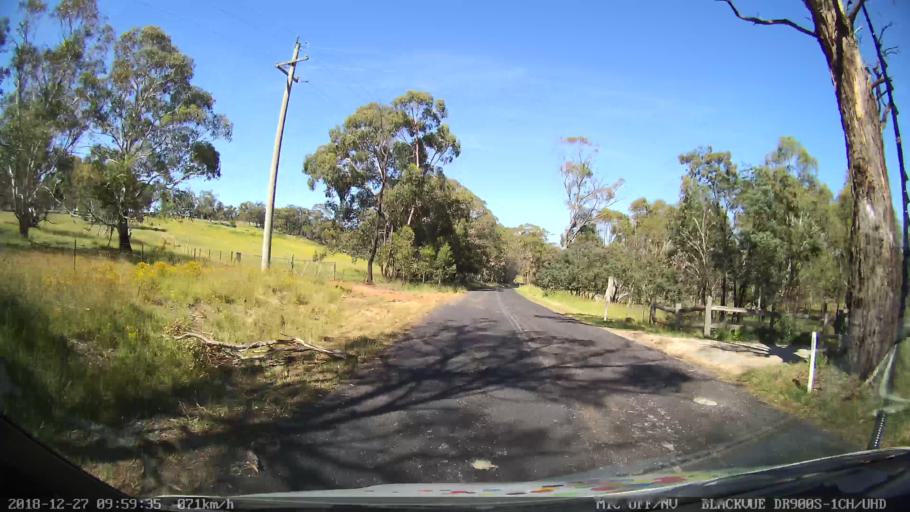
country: AU
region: New South Wales
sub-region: Lithgow
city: Portland
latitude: -33.4345
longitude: 149.9501
